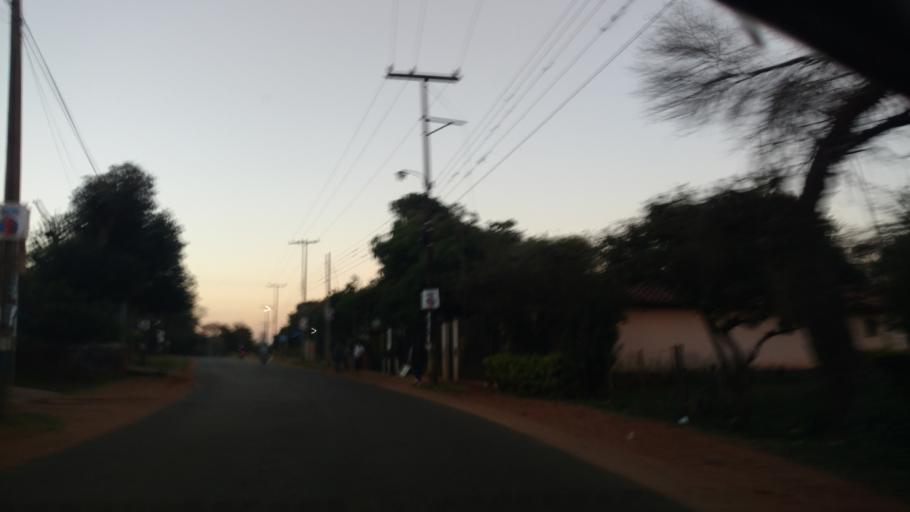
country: PY
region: Central
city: Guarambare
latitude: -25.4688
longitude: -57.4091
